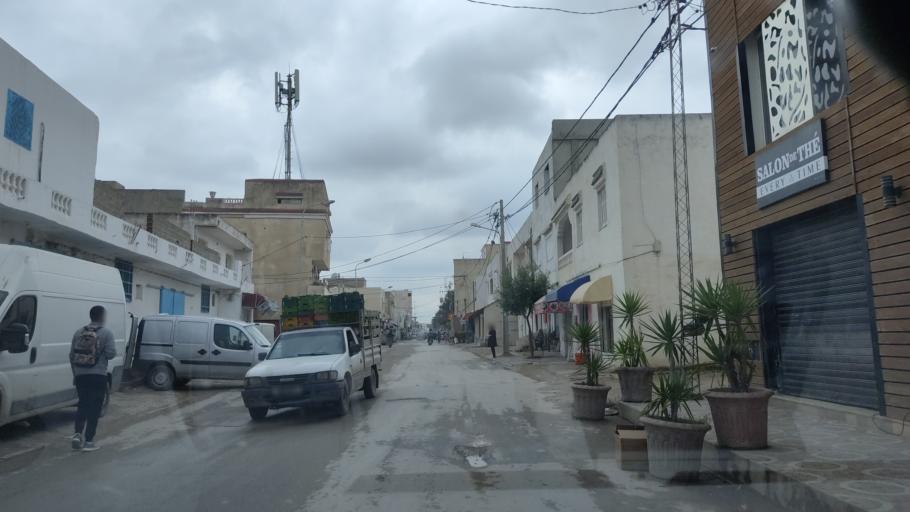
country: TN
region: Ariana
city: Ariana
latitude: 36.8749
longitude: 10.2186
